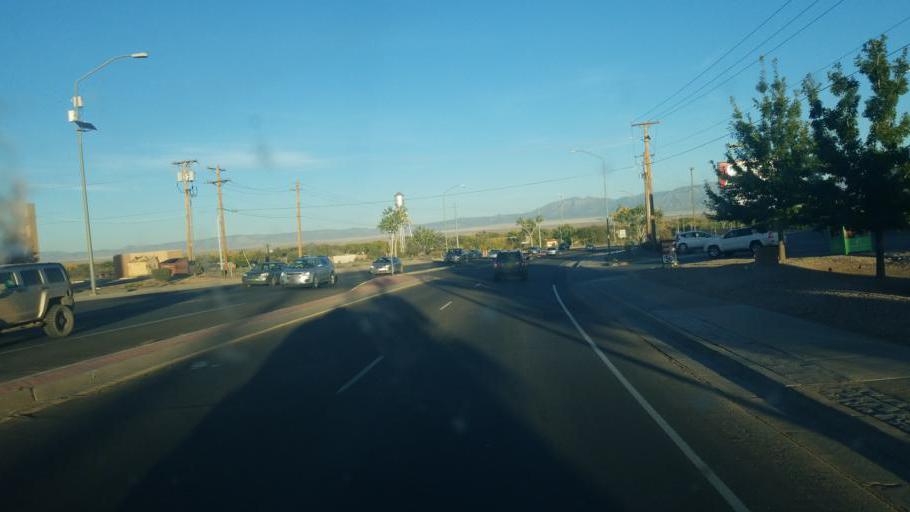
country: US
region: New Mexico
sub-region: Valencia County
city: Los Lunas
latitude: 34.8147
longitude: -106.7500
